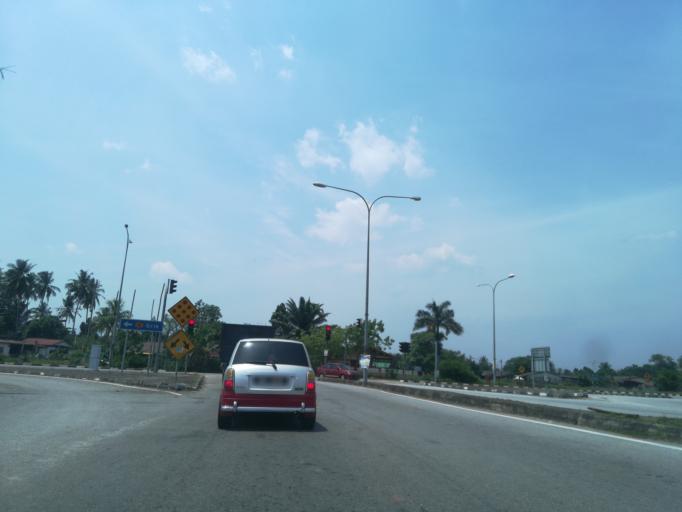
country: MY
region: Kedah
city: Kulim
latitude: 5.4342
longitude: 100.5520
